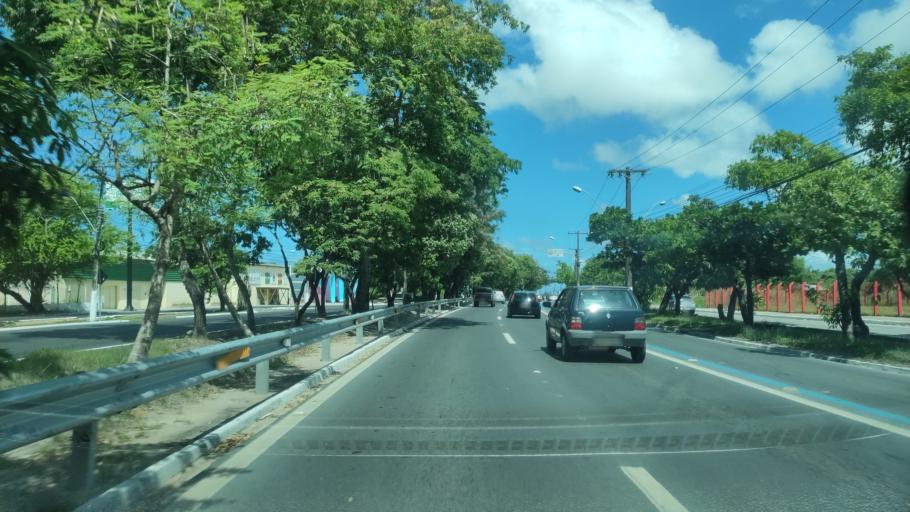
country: BR
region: Alagoas
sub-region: Maceio
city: Maceio
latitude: -9.5959
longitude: -35.7514
